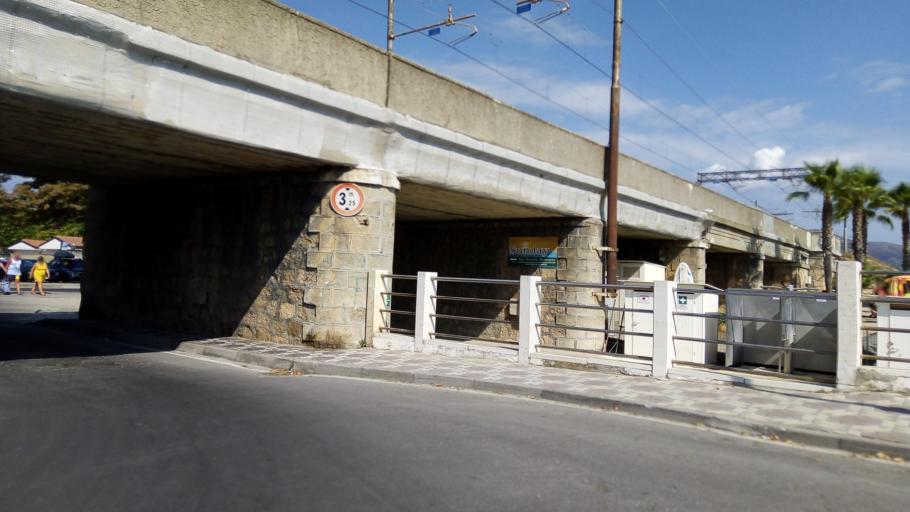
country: IT
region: Liguria
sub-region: Provincia di Savona
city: Albenga
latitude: 44.0532
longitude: 8.2258
